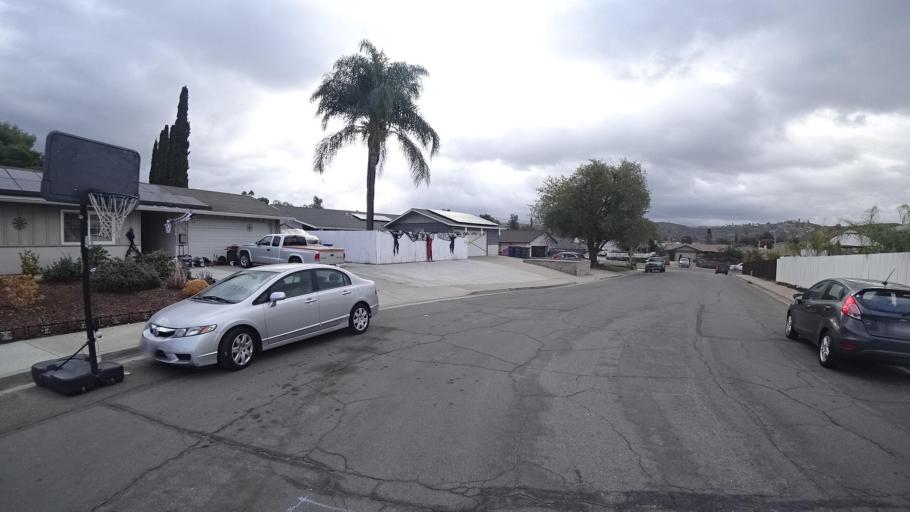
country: US
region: California
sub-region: San Diego County
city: Lakeside
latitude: 32.8636
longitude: -116.9105
